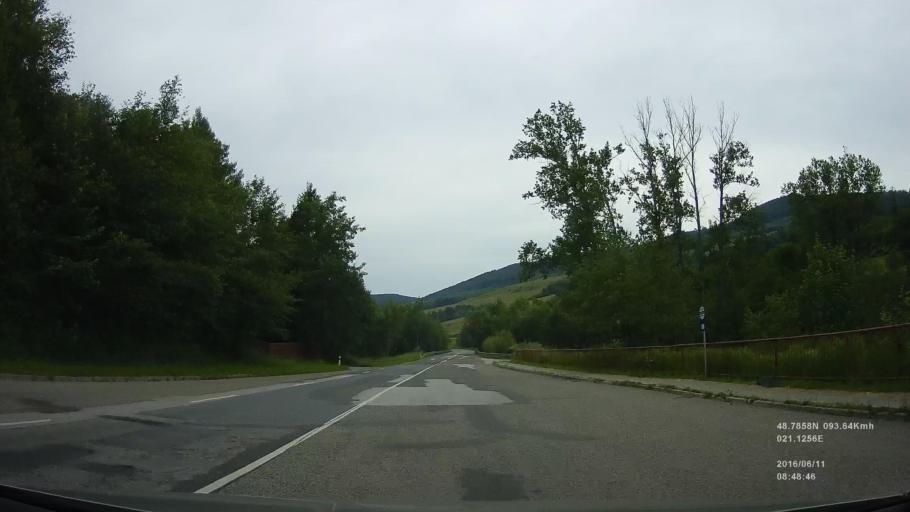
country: SK
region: Kosicky
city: Kosice
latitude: 48.7720
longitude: 21.1652
